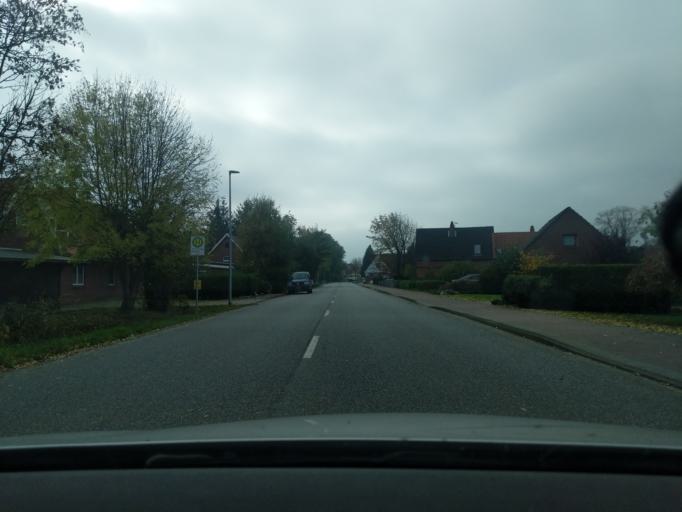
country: DE
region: Lower Saxony
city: Otterndorf
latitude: 53.8119
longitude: 8.9165
